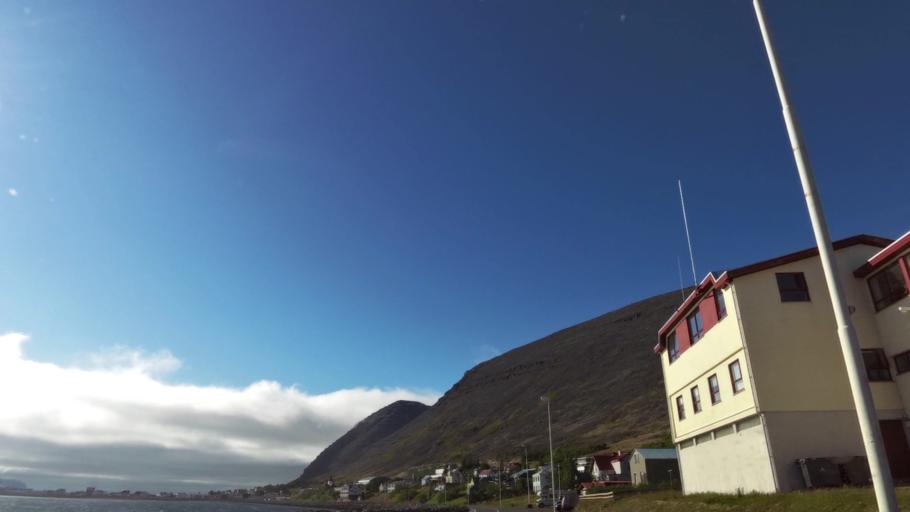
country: IS
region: West
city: Olafsvik
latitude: 65.5924
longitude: -23.9787
